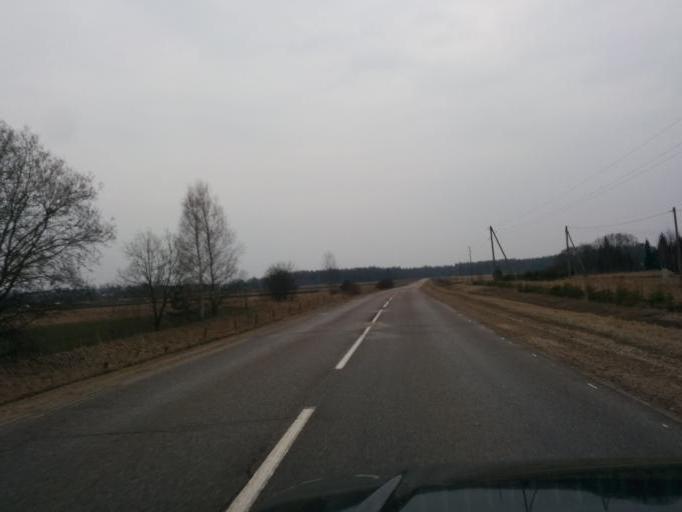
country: LV
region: Ikskile
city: Ikskile
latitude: 56.8202
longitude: 24.4496
